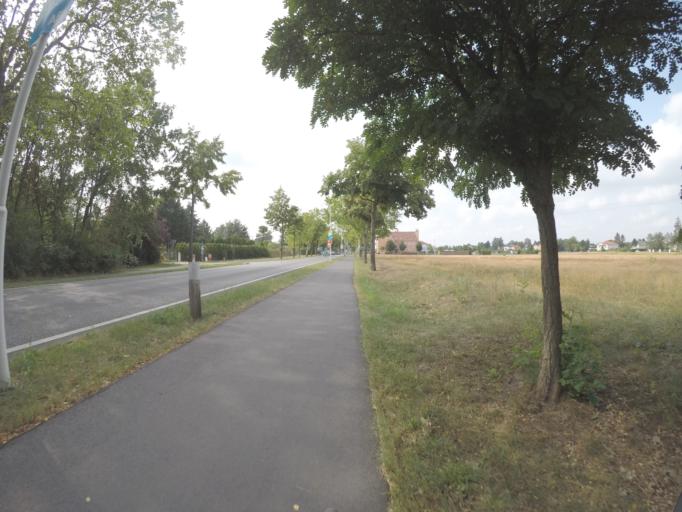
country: DE
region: Berlin
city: Lichtenrade
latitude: 52.3480
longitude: 13.4250
